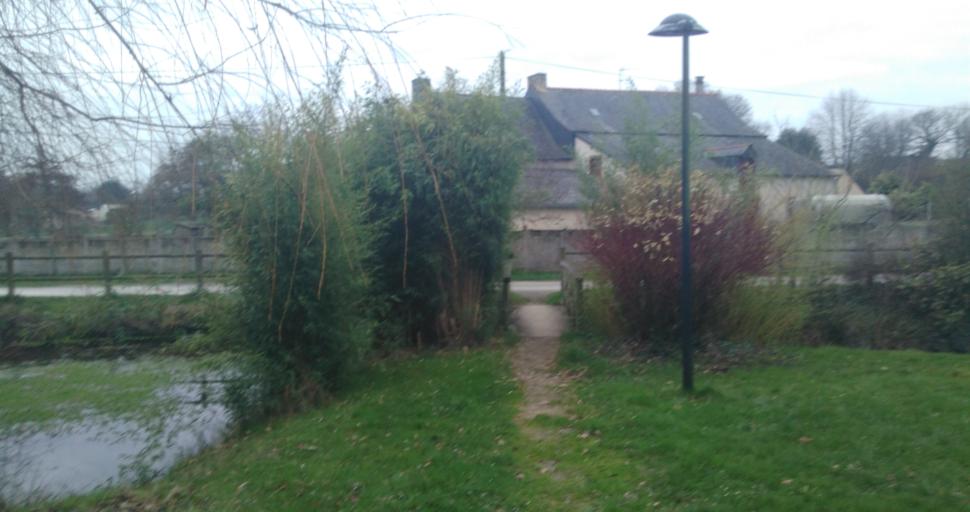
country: FR
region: Brittany
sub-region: Departement d'Ille-et-Vilaine
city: Romille
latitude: 48.2173
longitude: -1.8942
